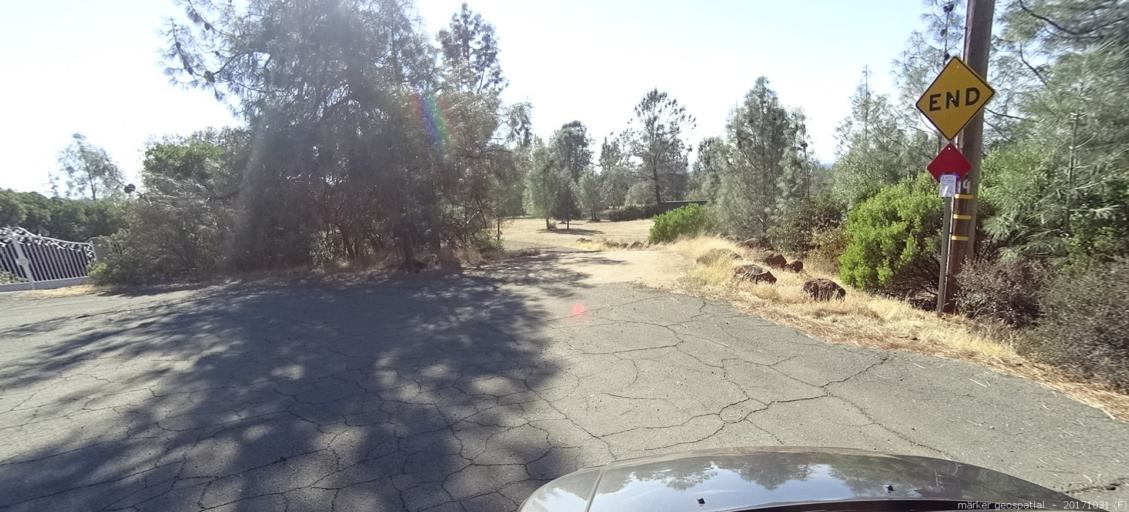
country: US
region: California
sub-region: Shasta County
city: Shingletown
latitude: 40.5089
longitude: -122.0290
